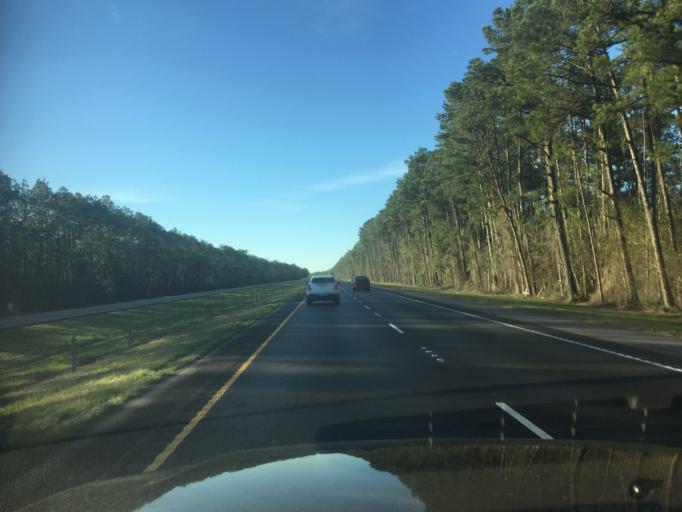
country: US
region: Louisiana
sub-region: Saint Tammany Parish
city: Lacombe
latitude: 30.3694
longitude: -89.9527
